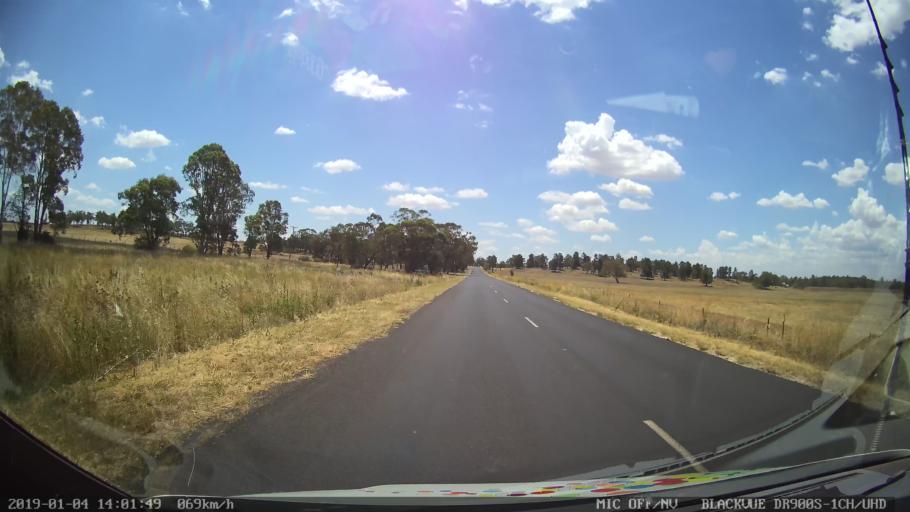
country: AU
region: New South Wales
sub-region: Dubbo Municipality
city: Dubbo
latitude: -32.2928
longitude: 148.5987
